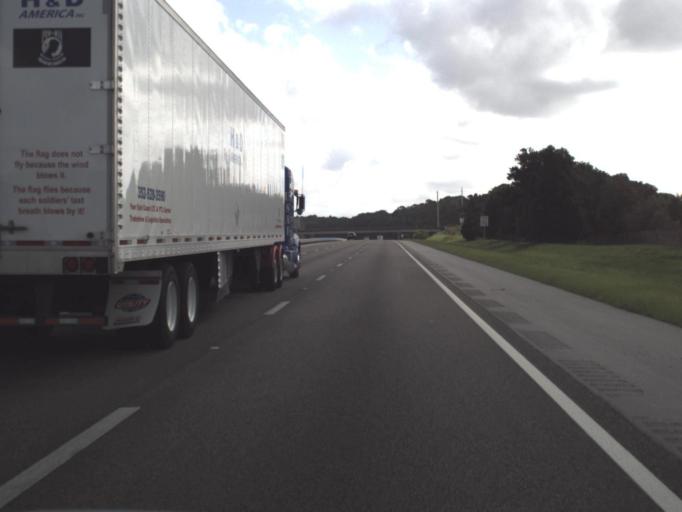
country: US
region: Florida
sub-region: Hillsborough County
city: University
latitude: 28.1056
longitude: -82.4349
